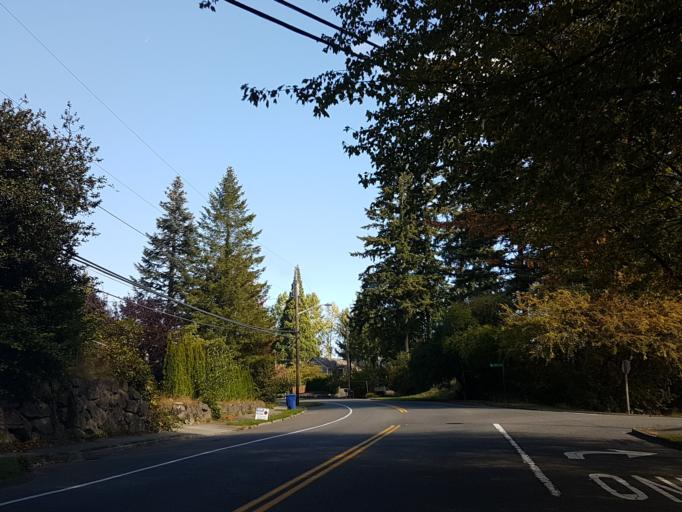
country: US
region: Washington
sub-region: Snohomish County
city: Brier
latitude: 47.7720
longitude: -122.2623
